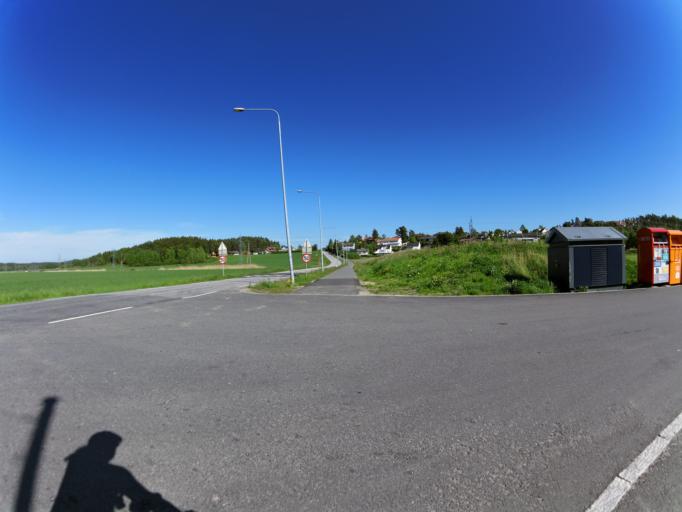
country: NO
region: Ostfold
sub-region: Fredrikstad
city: Fredrikstad
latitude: 59.2311
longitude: 11.0108
